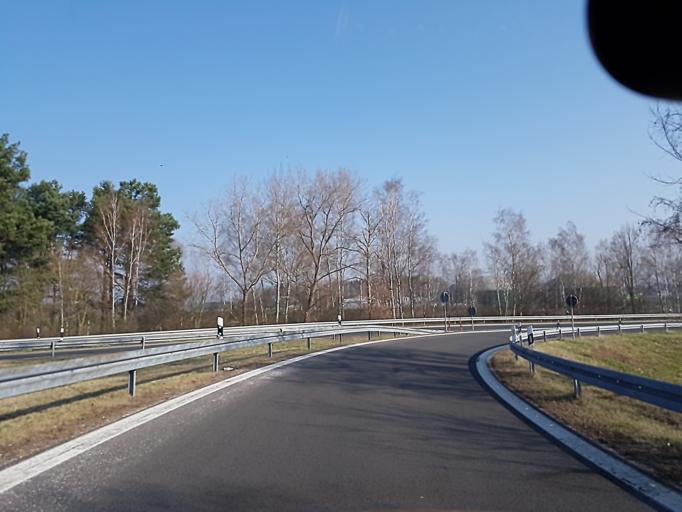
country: DE
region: Brandenburg
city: Forst
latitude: 51.7126
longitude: 14.6088
